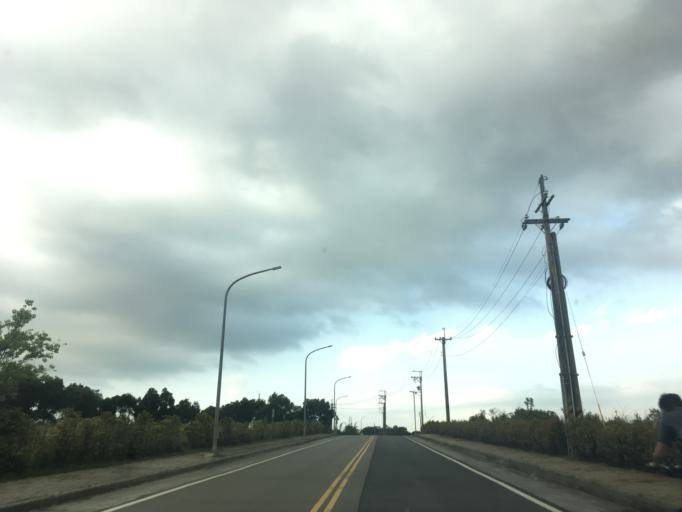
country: TW
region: Taiwan
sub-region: Taichung City
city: Taichung
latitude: 24.1739
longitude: 120.7679
